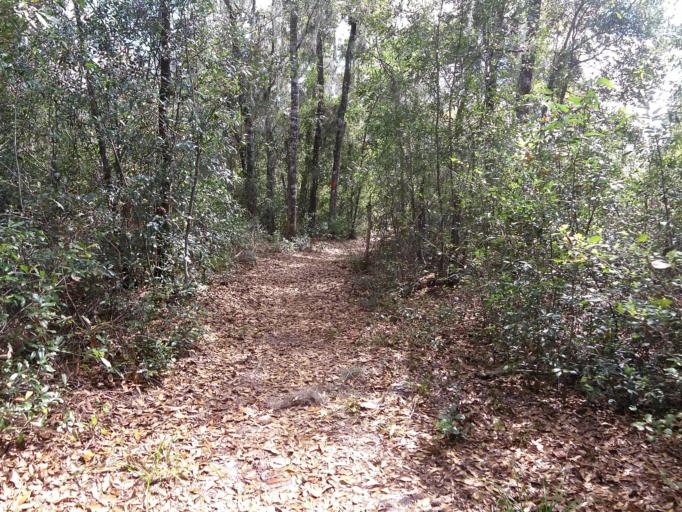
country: US
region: Florida
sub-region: Clay County
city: Keystone Heights
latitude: 29.7839
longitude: -81.8748
